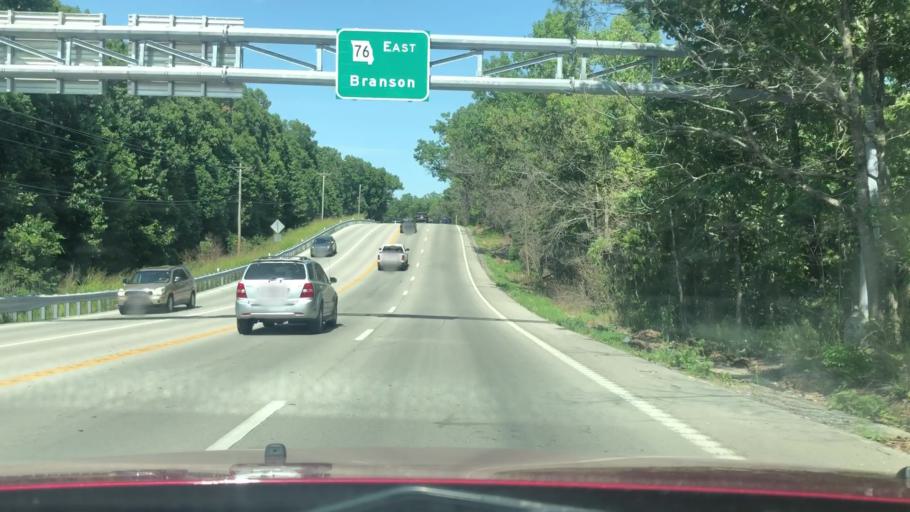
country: US
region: Missouri
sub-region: Stone County
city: Kimberling City
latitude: 36.6713
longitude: -93.3331
